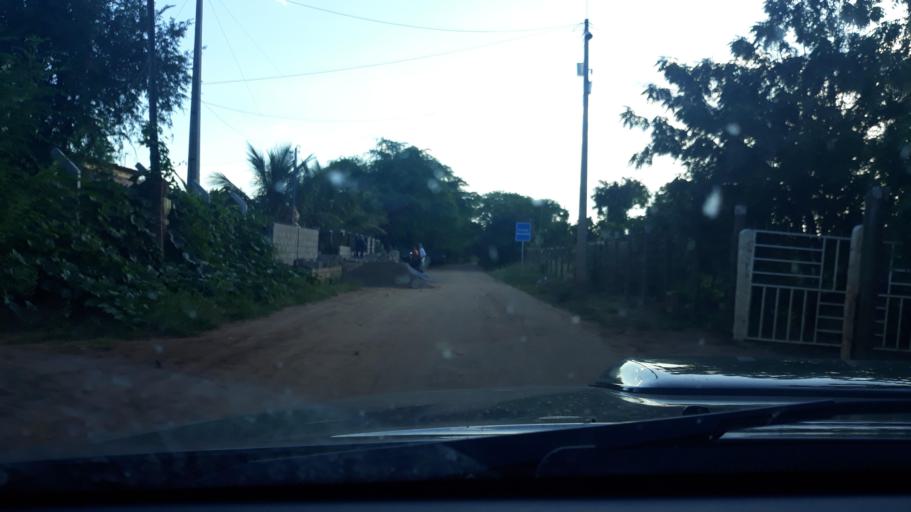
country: BR
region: Bahia
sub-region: Riacho De Santana
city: Riacho de Santana
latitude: -13.8083
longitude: -42.7172
